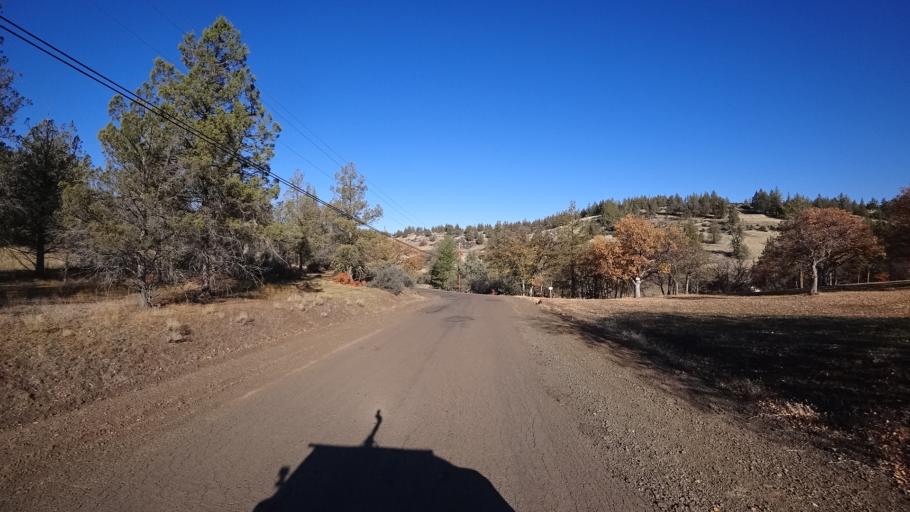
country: US
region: California
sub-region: Siskiyou County
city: Montague
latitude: 41.9138
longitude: -122.4335
